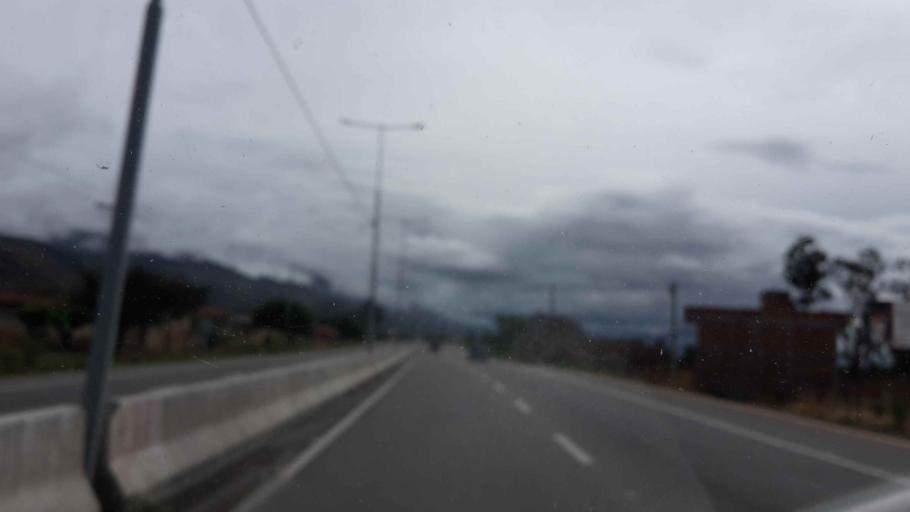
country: BO
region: Cochabamba
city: Tarata
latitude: -17.5416
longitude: -65.9947
